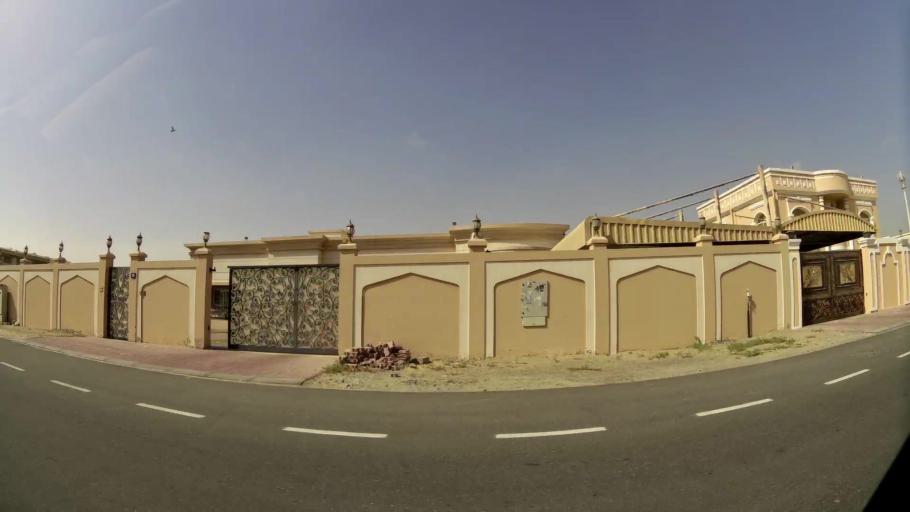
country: AE
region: Ash Shariqah
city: Sharjah
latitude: 25.2076
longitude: 55.4134
